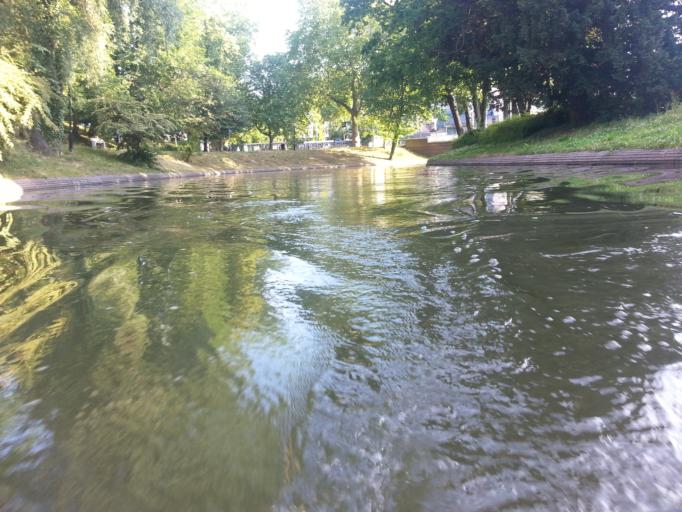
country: NL
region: Utrecht
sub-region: Gemeente Utrecht
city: Utrecht
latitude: 52.0920
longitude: 5.1272
